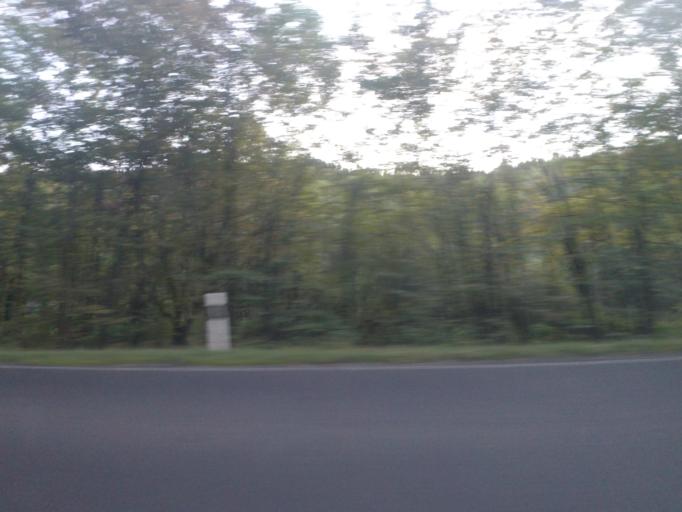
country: DE
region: Hesse
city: Hain-Grundau
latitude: 50.2581
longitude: 9.1966
